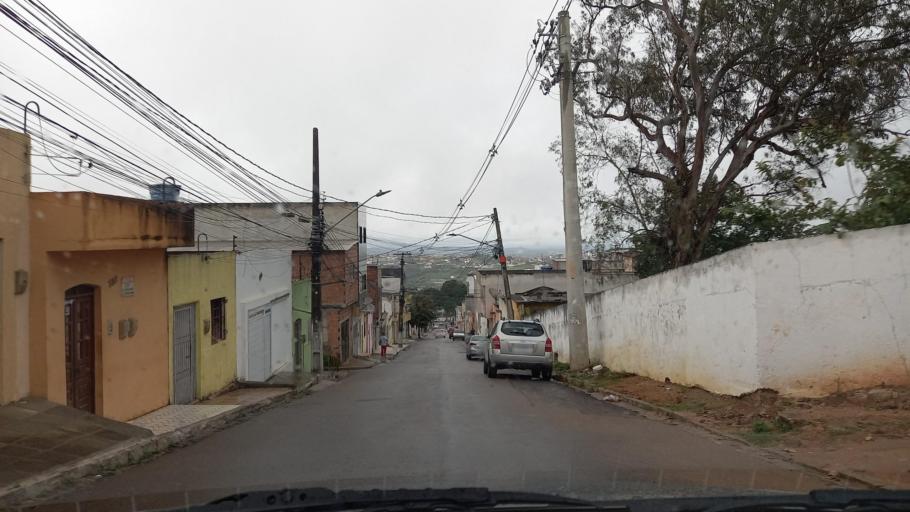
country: BR
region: Pernambuco
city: Garanhuns
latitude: -8.8852
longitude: -36.4943
